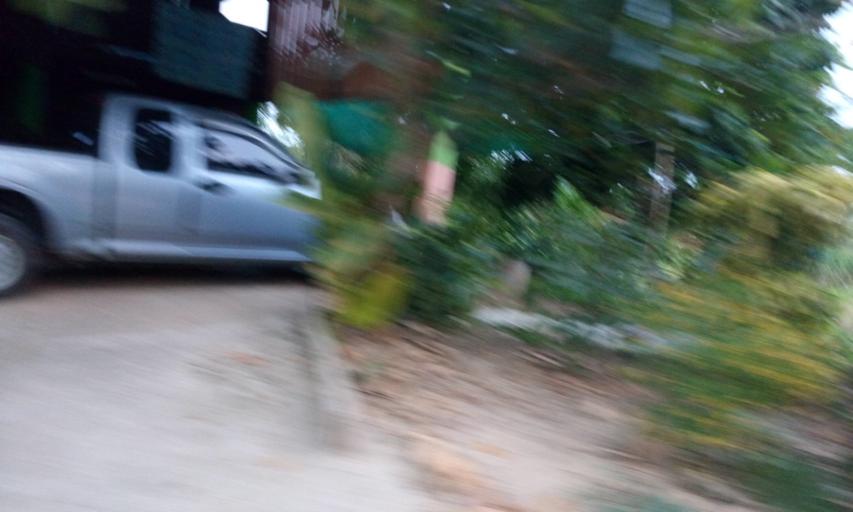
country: TH
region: Phayao
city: Phu Sang
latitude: 19.6129
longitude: 100.3267
